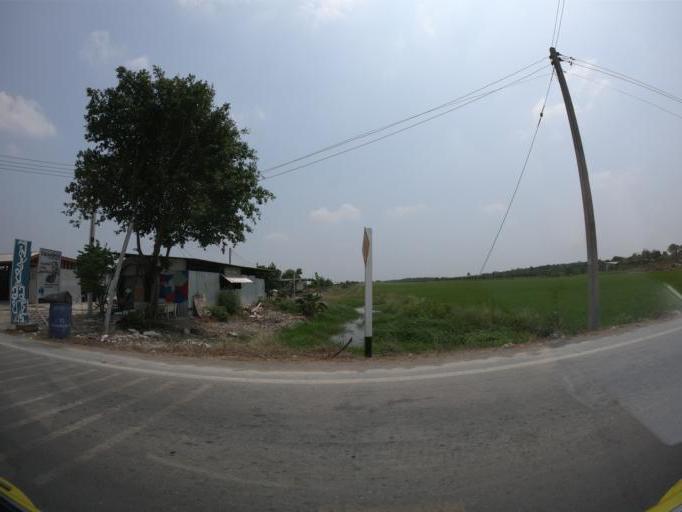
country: TH
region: Pathum Thani
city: Ban Lam Luk Ka
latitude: 13.9761
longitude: 100.8198
